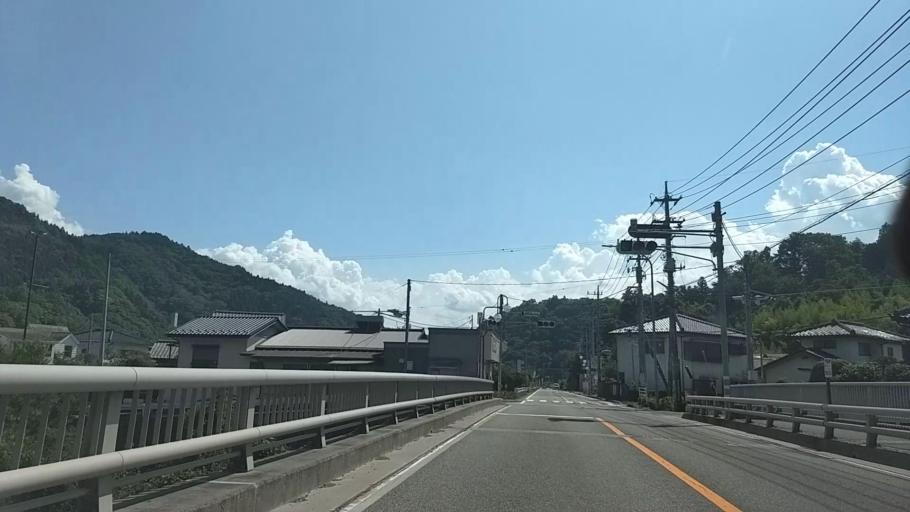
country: JP
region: Yamanashi
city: Ryuo
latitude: 35.4762
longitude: 138.4446
